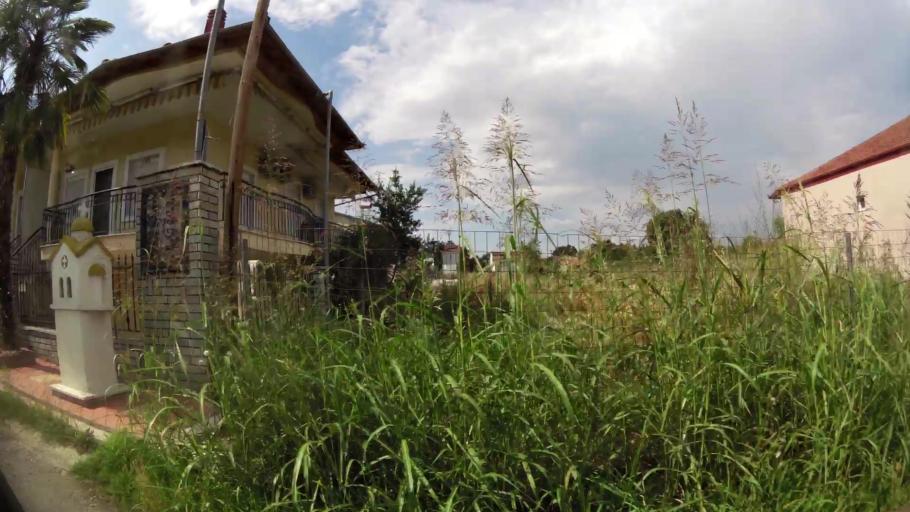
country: GR
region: Central Macedonia
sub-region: Nomos Pierias
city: Makrygialos
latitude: 40.4112
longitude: 22.6057
